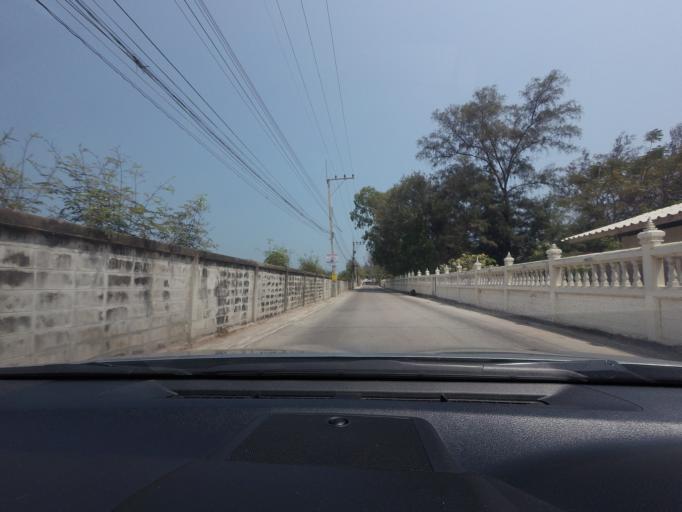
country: TH
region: Phetchaburi
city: Cha-am
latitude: 12.8146
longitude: 99.9912
